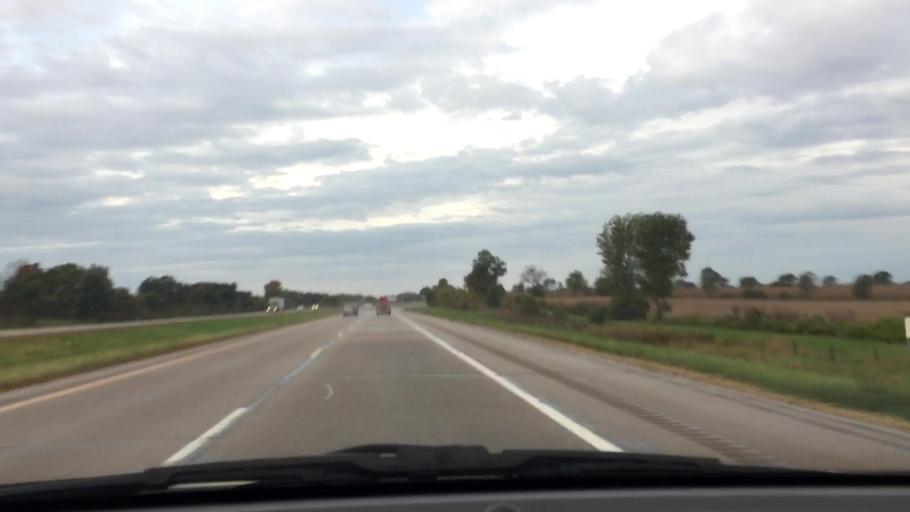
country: US
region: Wisconsin
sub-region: Rock County
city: Clinton
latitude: 42.5753
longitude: -88.8016
